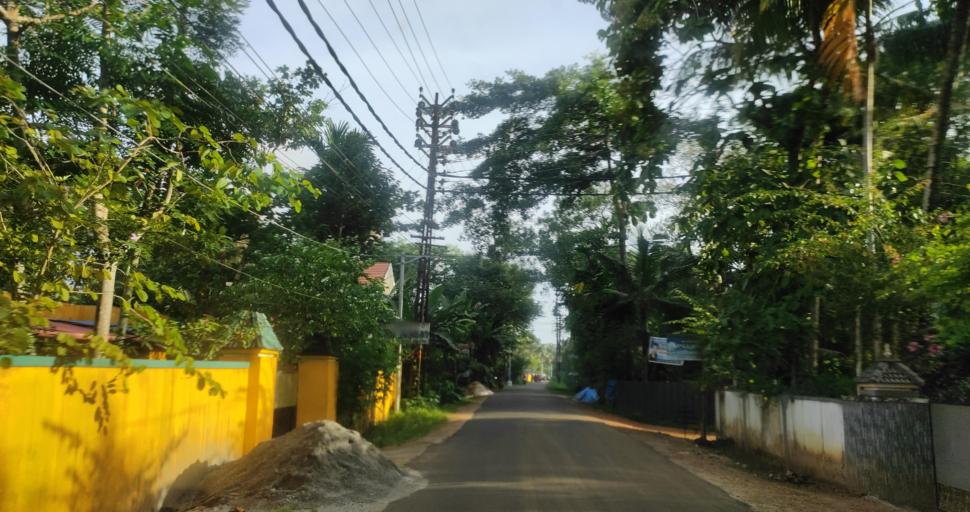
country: IN
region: Kerala
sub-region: Alappuzha
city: Shertallai
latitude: 9.6433
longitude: 76.3448
